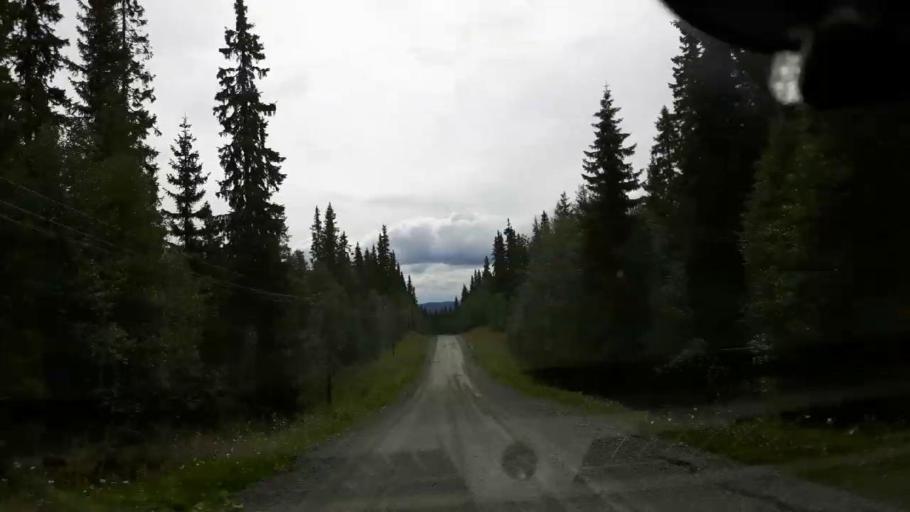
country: SE
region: Jaemtland
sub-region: Krokoms Kommun
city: Valla
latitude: 63.7173
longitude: 13.8588
